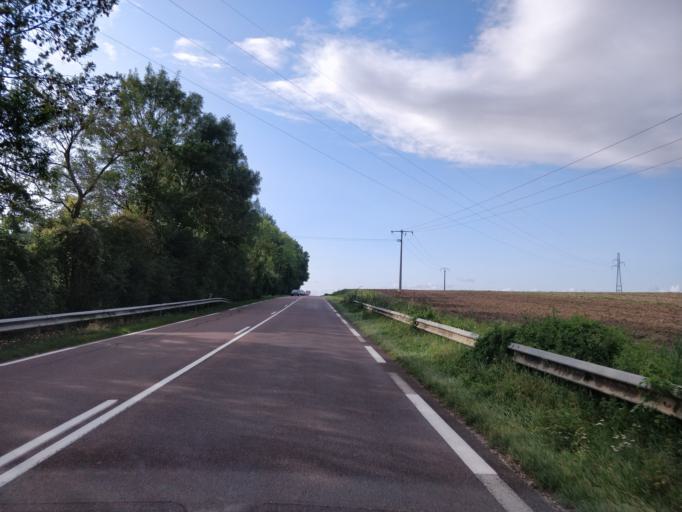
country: FR
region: Champagne-Ardenne
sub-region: Departement de l'Aube
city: Lusigny-sur-Barse
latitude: 48.2707
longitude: 4.2089
